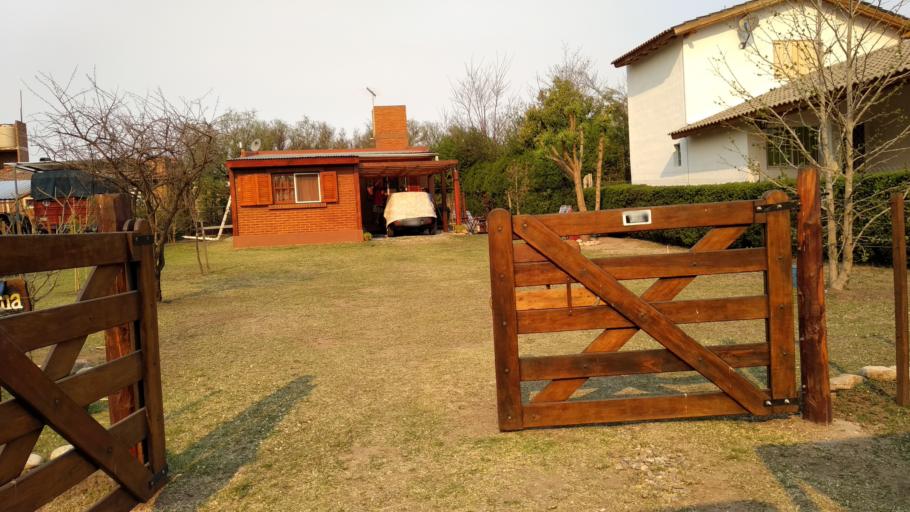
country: AR
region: Cordoba
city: Mina Clavero
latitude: -31.7706
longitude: -65.0017
